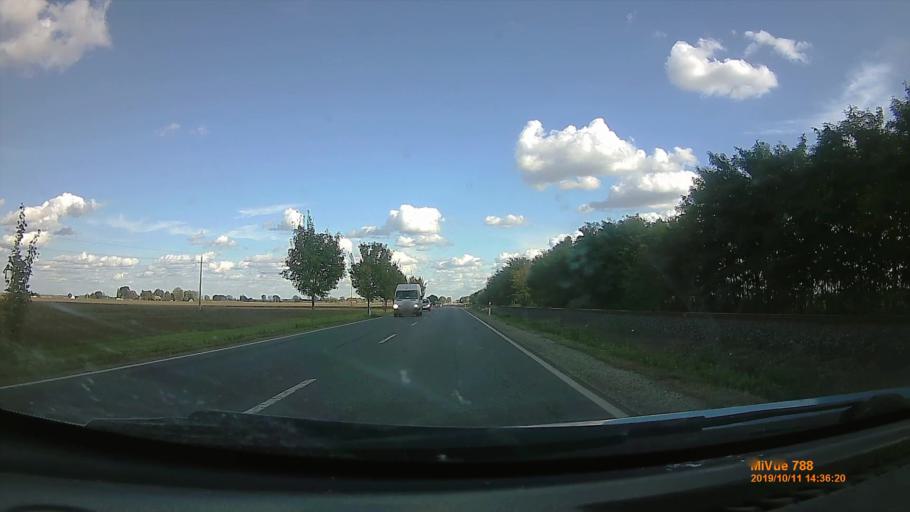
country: HU
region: Hajdu-Bihar
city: Ebes
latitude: 47.5572
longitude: 21.5068
